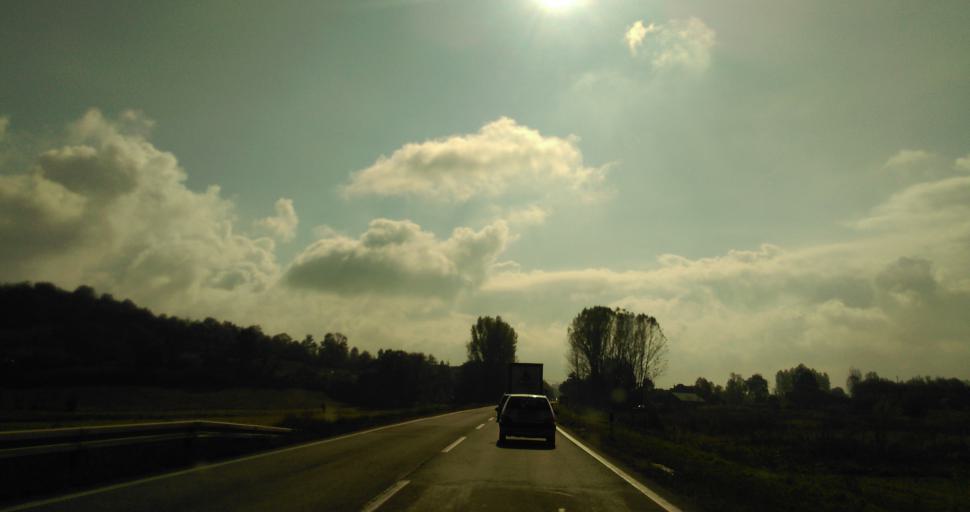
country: RS
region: Central Serbia
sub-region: Kolubarski Okrug
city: Lajkovac
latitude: 44.3397
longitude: 20.2085
